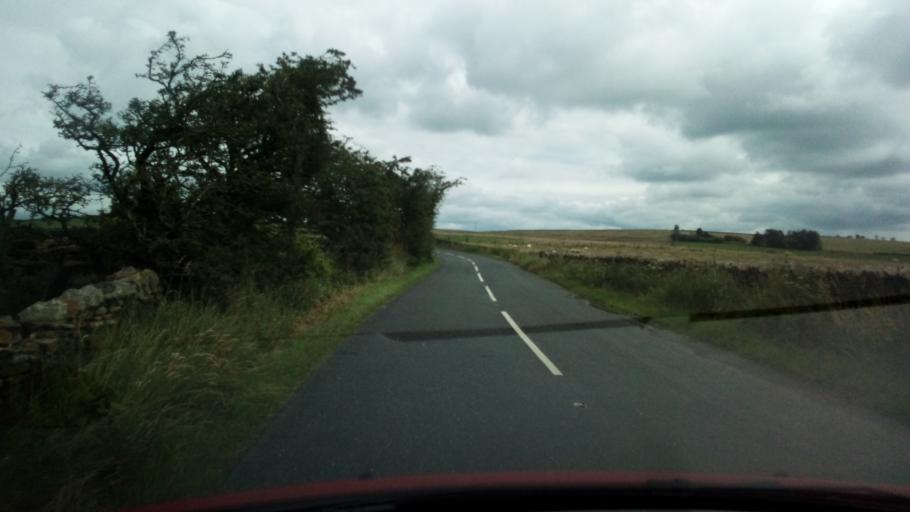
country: GB
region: England
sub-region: Lancashire
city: Clitheroe
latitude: 53.9696
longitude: -2.4087
